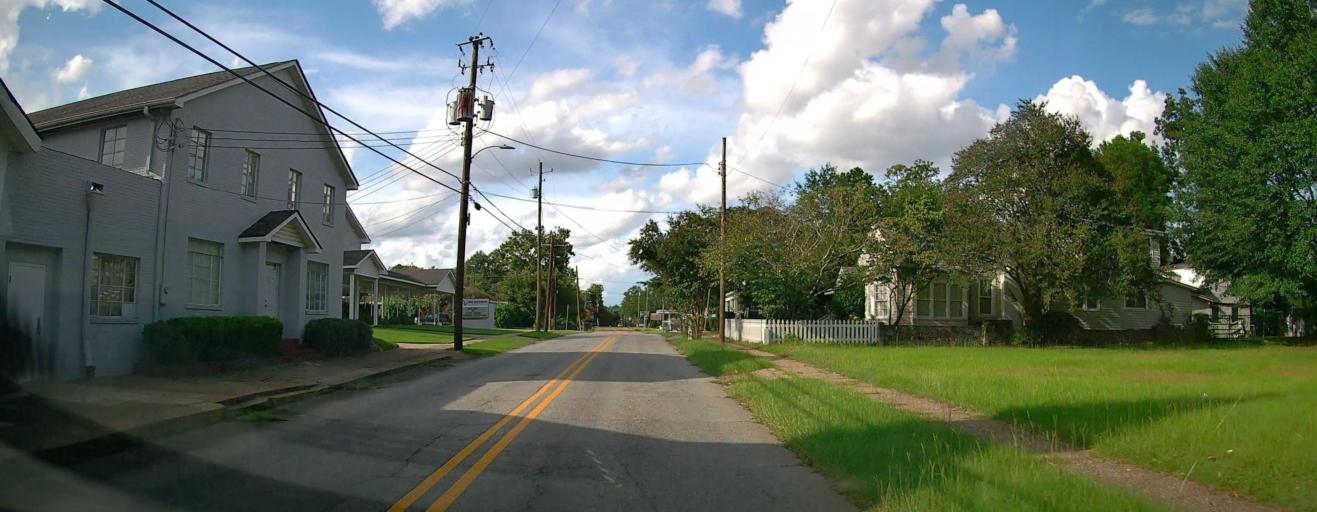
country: US
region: Alabama
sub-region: Russell County
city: Phenix City
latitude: 32.4808
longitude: -84.9986
